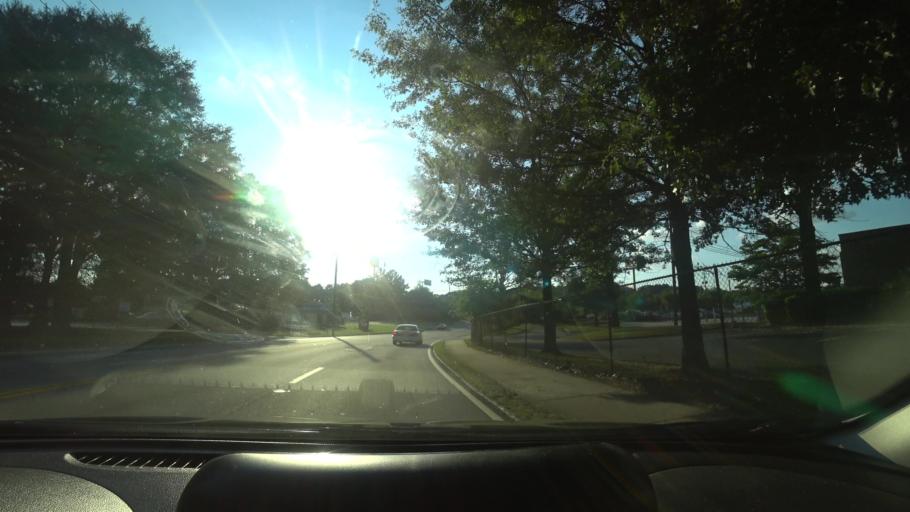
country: US
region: Georgia
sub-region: Fulton County
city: Atlanta
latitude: 33.7212
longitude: -84.3914
